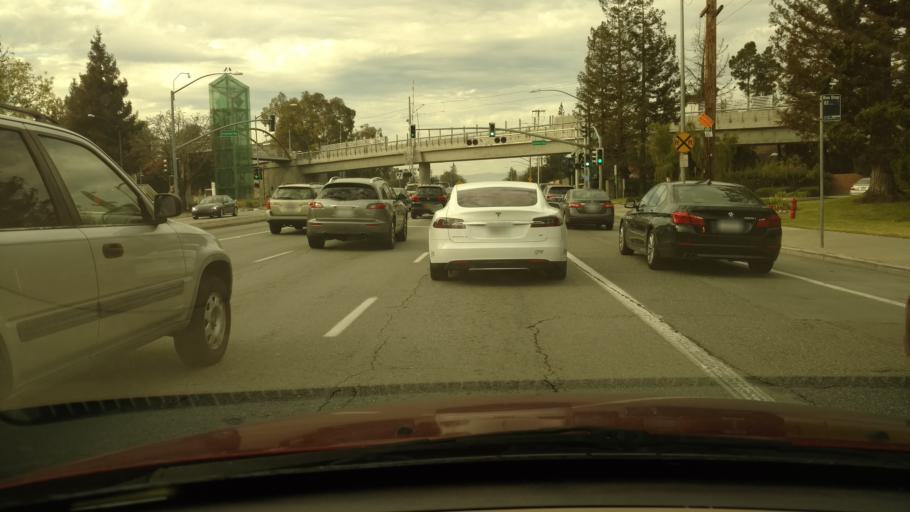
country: US
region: California
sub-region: Santa Clara County
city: Campbell
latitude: 37.2944
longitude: -121.9348
